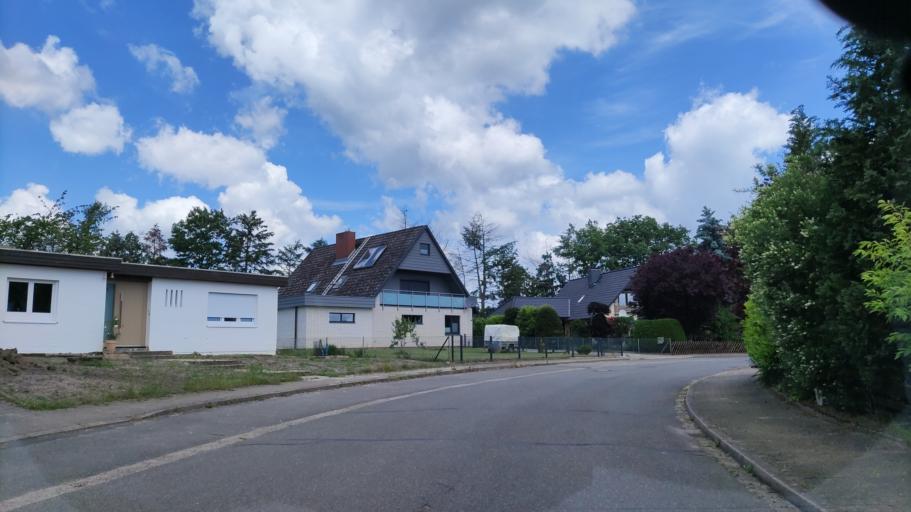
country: DE
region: Lower Saxony
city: Deutsch Evern
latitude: 53.1965
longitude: 10.4301
